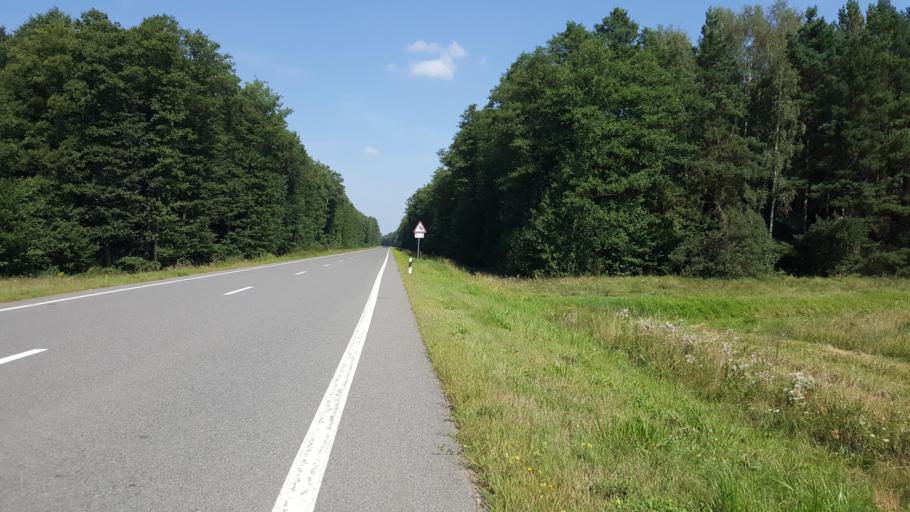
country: BY
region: Brest
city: Kamyanyuki
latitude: 52.5283
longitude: 23.6557
